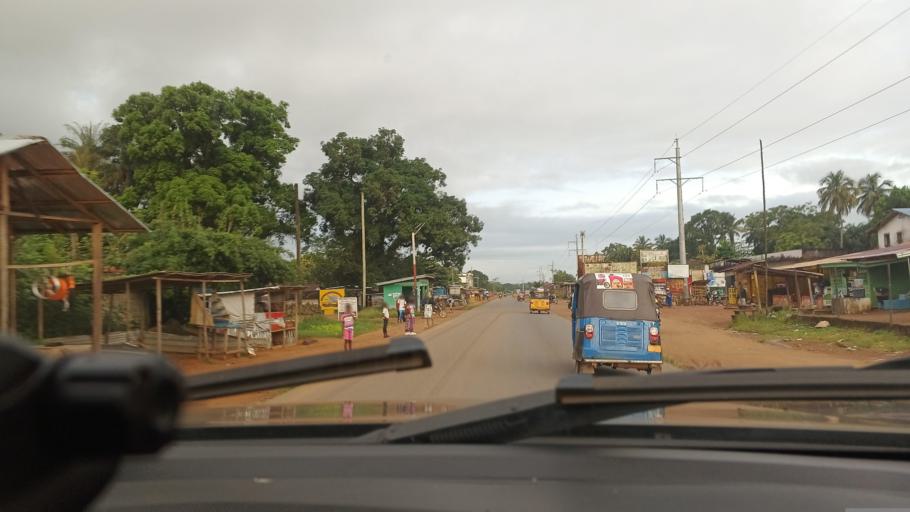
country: LR
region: Montserrado
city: Monrovia
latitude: 6.4472
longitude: -10.8001
